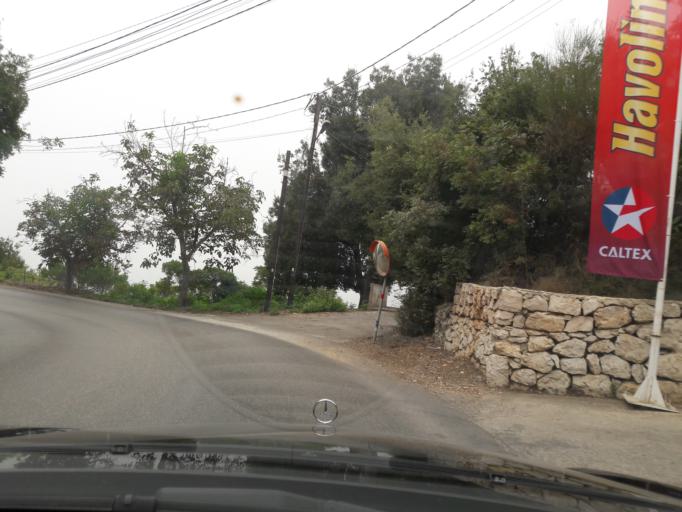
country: LB
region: Mont-Liban
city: Djounie
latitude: 33.9892
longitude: 35.6796
